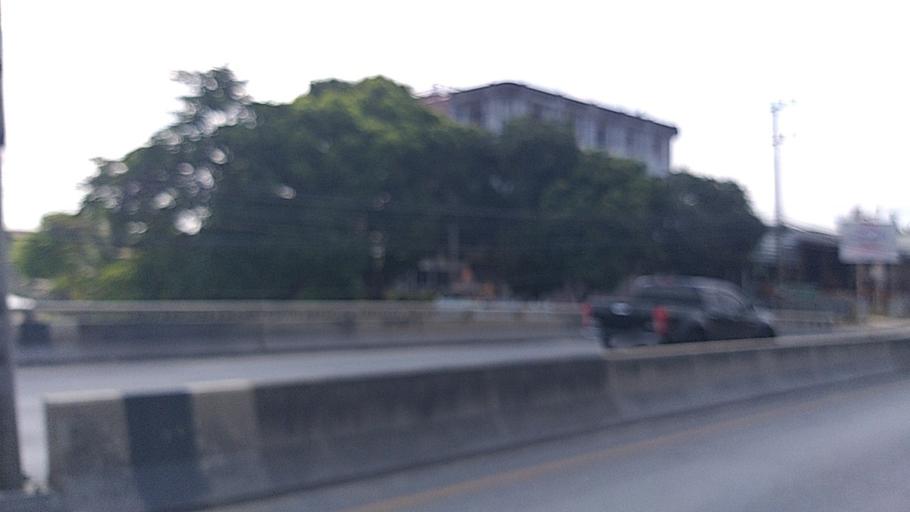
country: TH
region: Pathum Thani
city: Sam Khok
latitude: 14.0687
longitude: 100.5229
